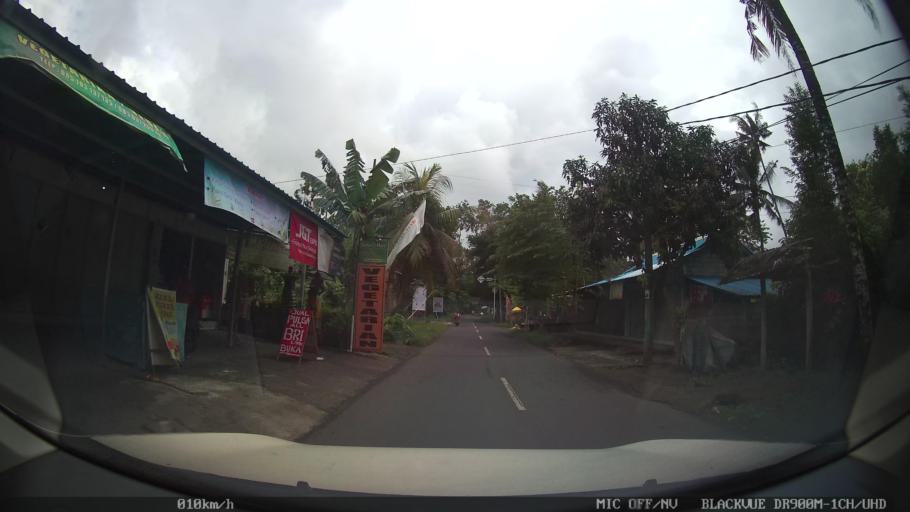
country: ID
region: Bali
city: Banjar Parekan
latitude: -8.5778
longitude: 115.2114
